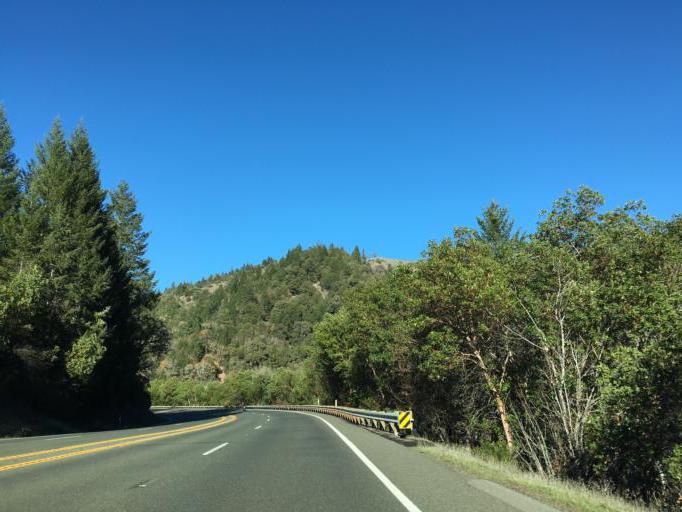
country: US
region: California
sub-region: Mendocino County
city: Laytonville
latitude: 39.6003
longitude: -123.4541
